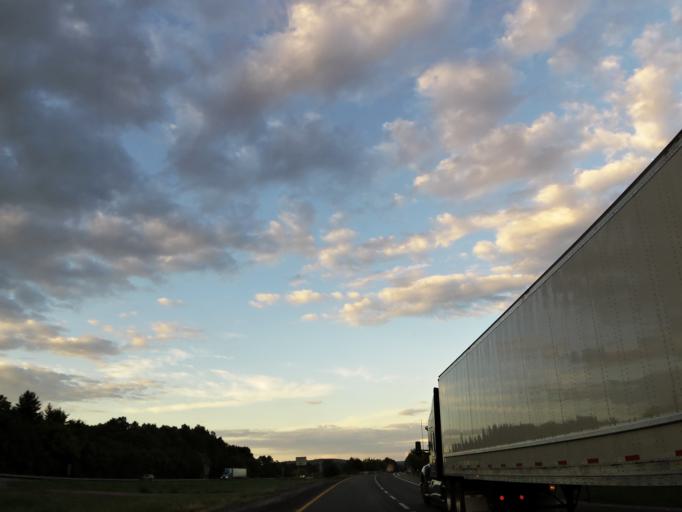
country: US
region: Tennessee
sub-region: Bradley County
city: Hopewell
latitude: 35.3129
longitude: -84.8035
